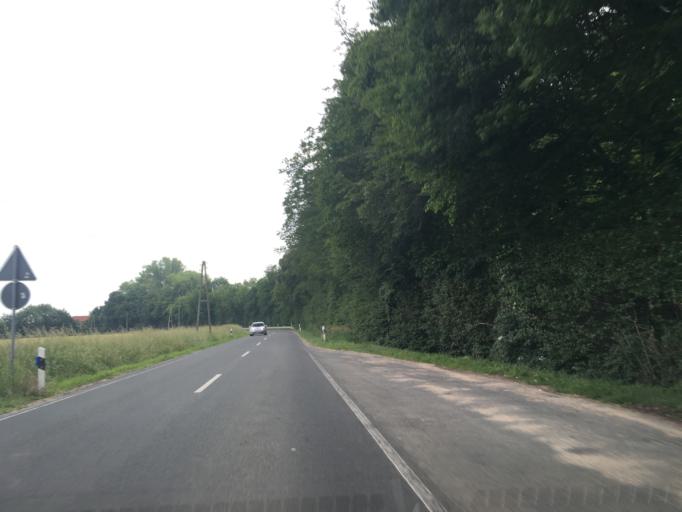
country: DE
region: North Rhine-Westphalia
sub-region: Regierungsbezirk Munster
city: Laer
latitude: 52.0851
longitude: 7.3445
